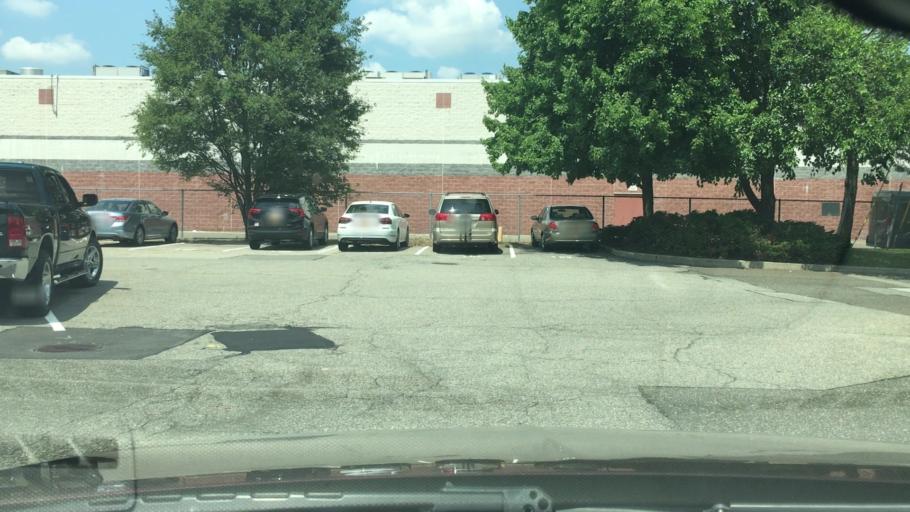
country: US
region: New York
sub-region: Suffolk County
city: East Farmingdale
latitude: 40.7464
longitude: -73.4288
